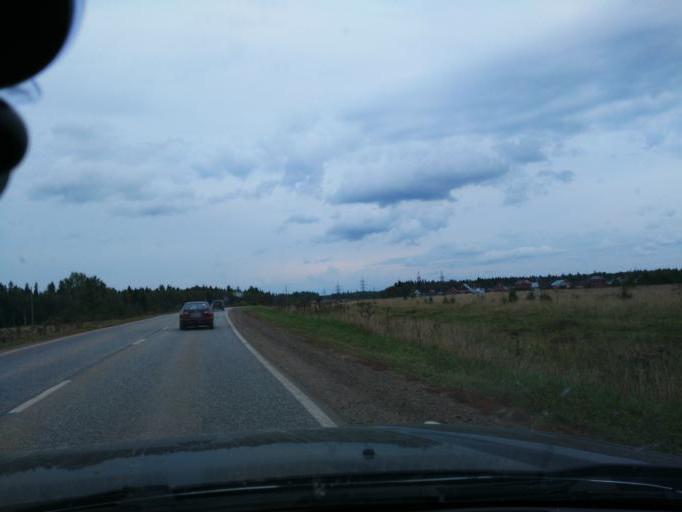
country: RU
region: Perm
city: Chernushka
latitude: 56.5276
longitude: 56.0291
